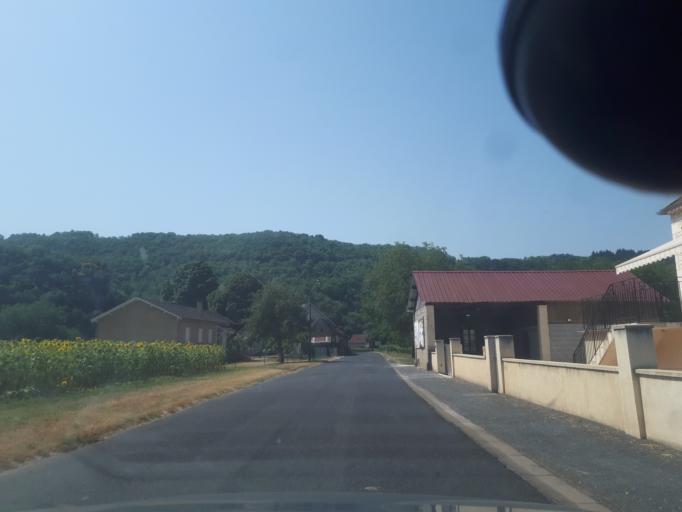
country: FR
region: Midi-Pyrenees
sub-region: Departement du Lot
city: Souillac
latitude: 44.8691
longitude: 1.4418
